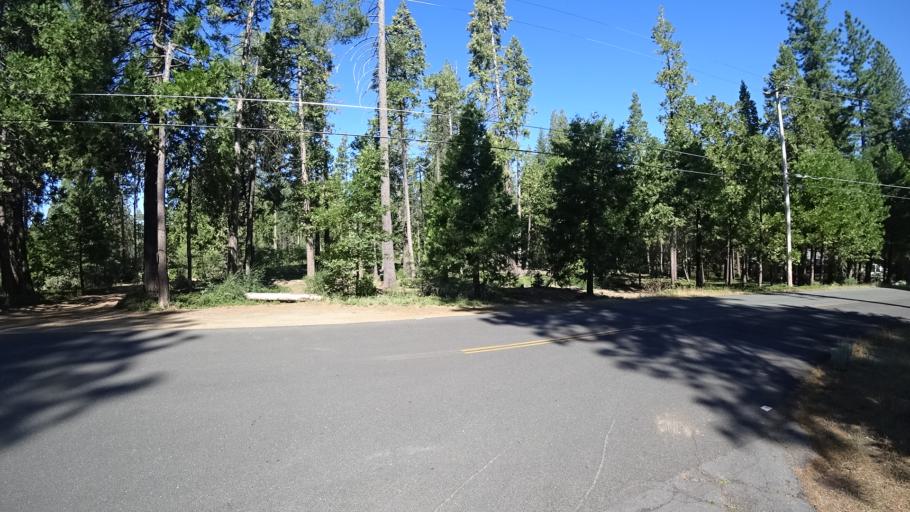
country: US
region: California
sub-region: Calaveras County
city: Arnold
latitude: 38.2518
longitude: -120.3725
